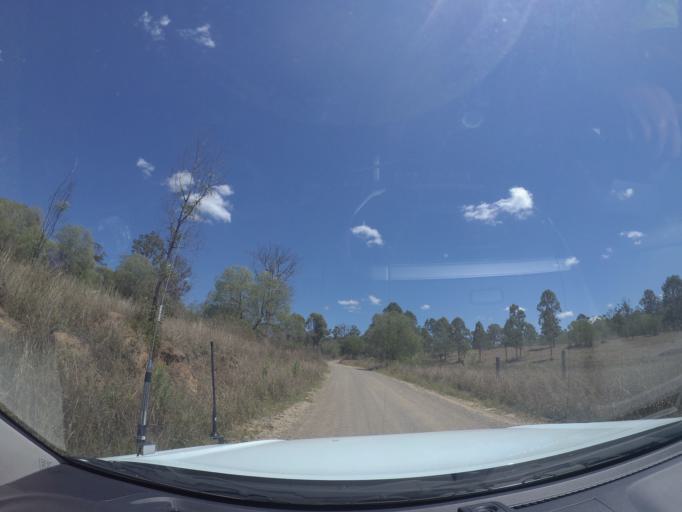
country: AU
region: Queensland
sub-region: Ipswich
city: Springfield Lakes
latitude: -27.8166
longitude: 152.8556
